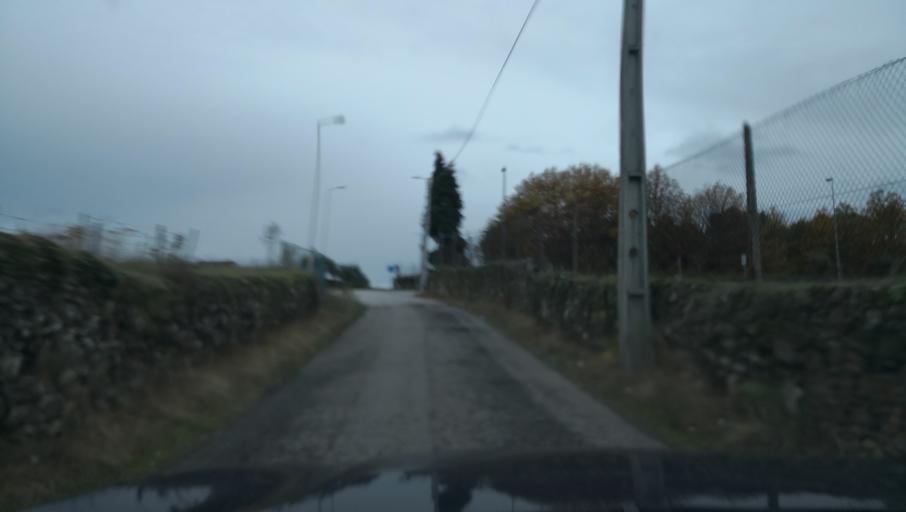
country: PT
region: Vila Real
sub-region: Vila Real
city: Vila Real
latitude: 41.2851
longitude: -7.7385
